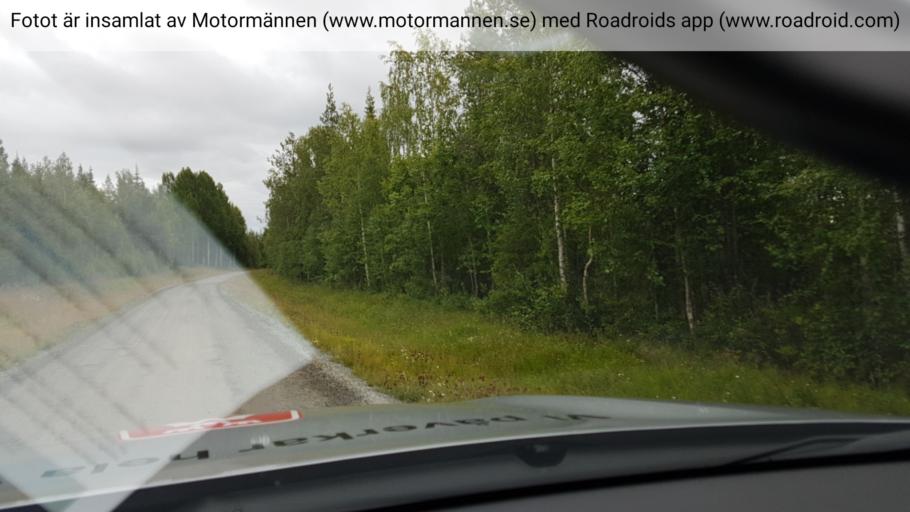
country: SE
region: Norrbotten
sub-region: Pajala Kommun
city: Pajala
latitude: 66.9748
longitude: 22.9061
